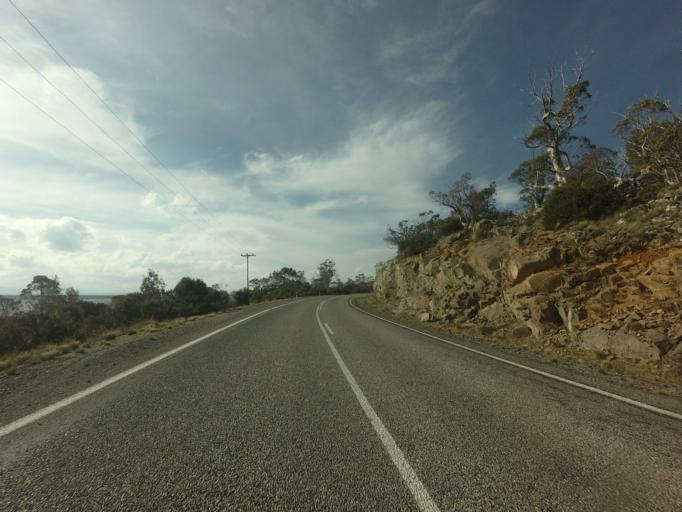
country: AU
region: Tasmania
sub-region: Meander Valley
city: Deloraine
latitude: -41.9868
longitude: 146.7109
